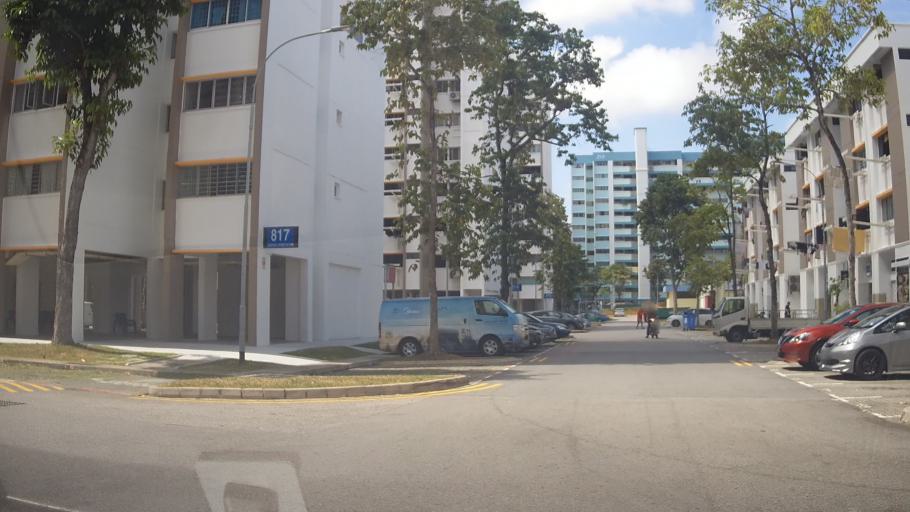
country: SG
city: Singapore
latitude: 1.3480
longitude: 103.9364
